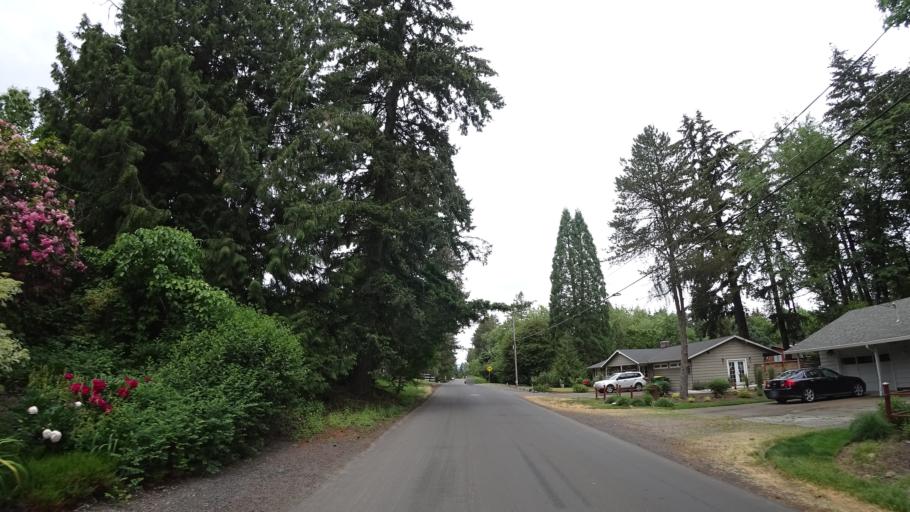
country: US
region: Oregon
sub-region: Washington County
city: Garden Home-Whitford
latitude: 45.4614
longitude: -122.7659
